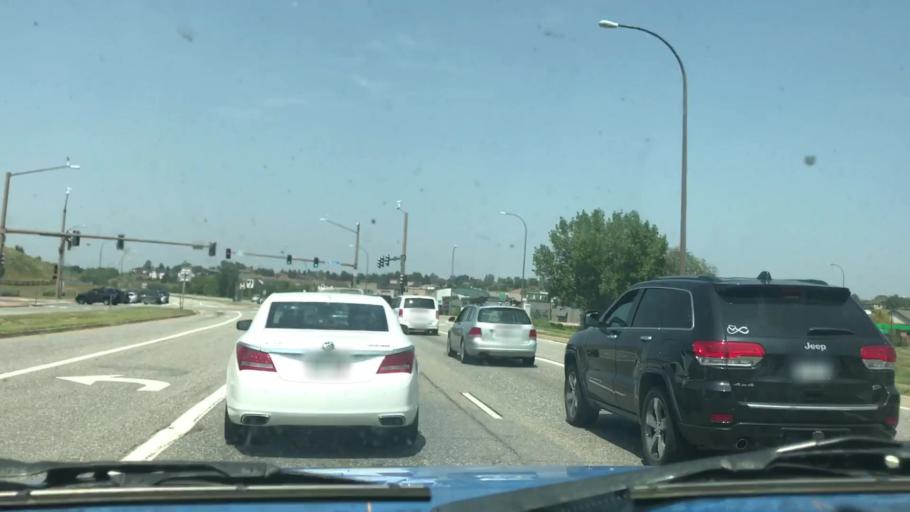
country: US
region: Colorado
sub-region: Jefferson County
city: Lakewood
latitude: 39.6668
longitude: -105.1149
